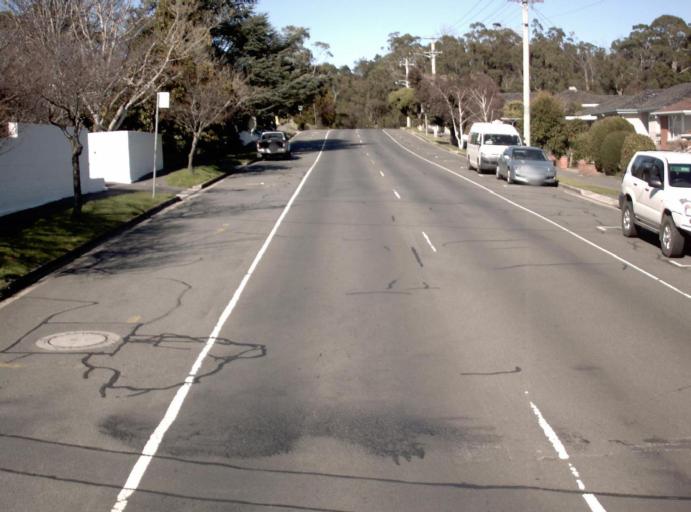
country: AU
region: Tasmania
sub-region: Launceston
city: East Launceston
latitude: -41.4531
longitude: 147.1641
